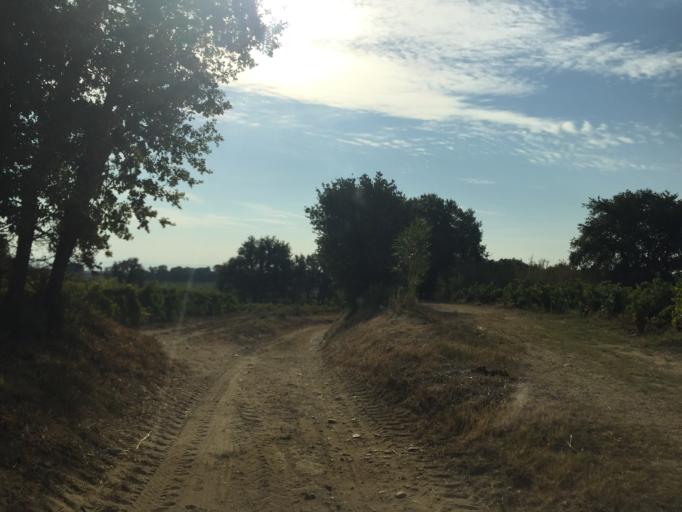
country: FR
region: Provence-Alpes-Cote d'Azur
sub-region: Departement du Vaucluse
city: Courthezon
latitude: 44.0786
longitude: 4.8597
